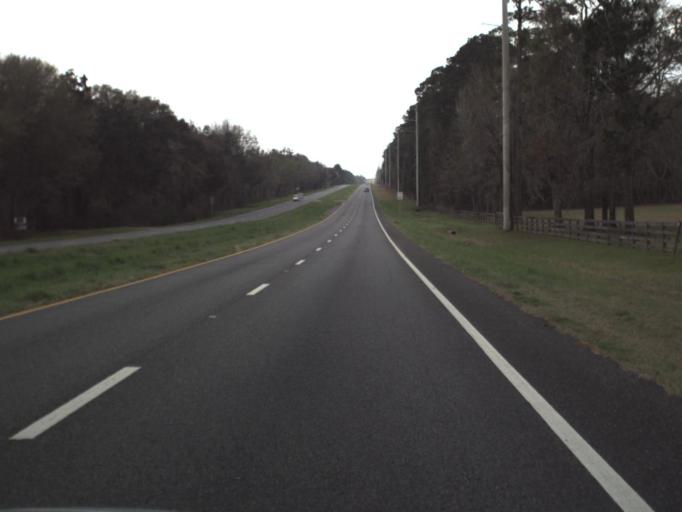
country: US
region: Florida
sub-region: Jefferson County
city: Monticello
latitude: 30.4042
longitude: -84.0275
